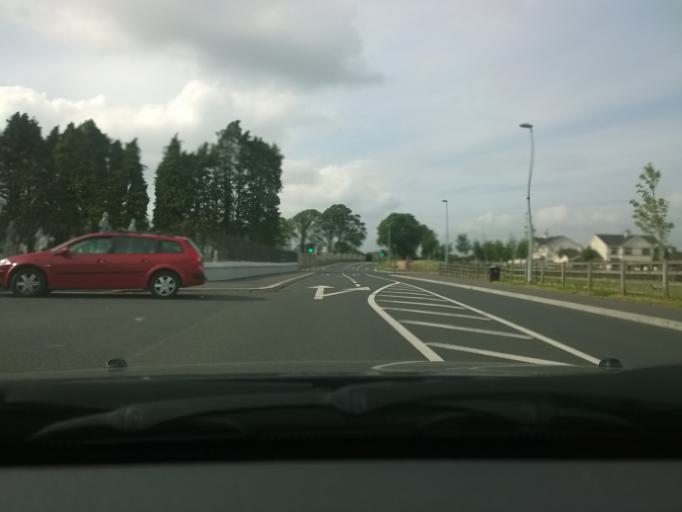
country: IE
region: Leinster
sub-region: Kildare
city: Kildare
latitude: 53.1691
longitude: -6.9129
